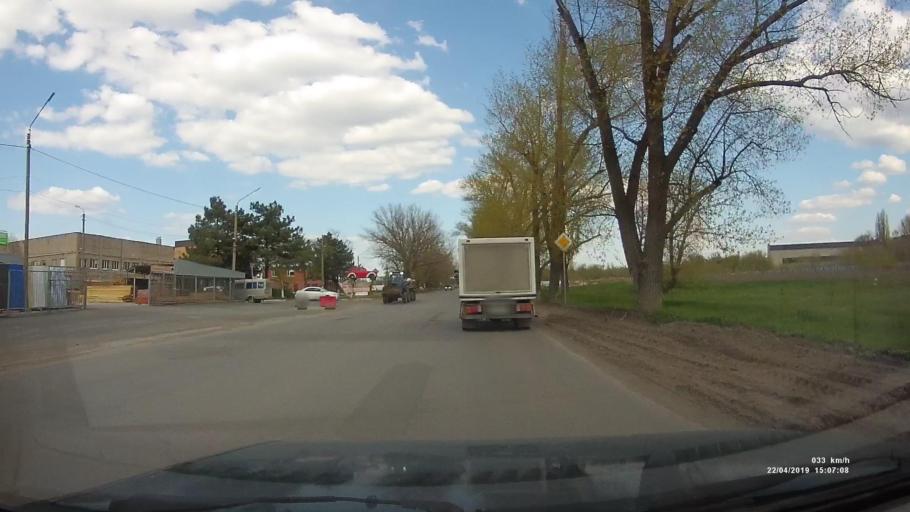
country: RU
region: Rostov
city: Azov
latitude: 47.0944
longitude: 39.4014
